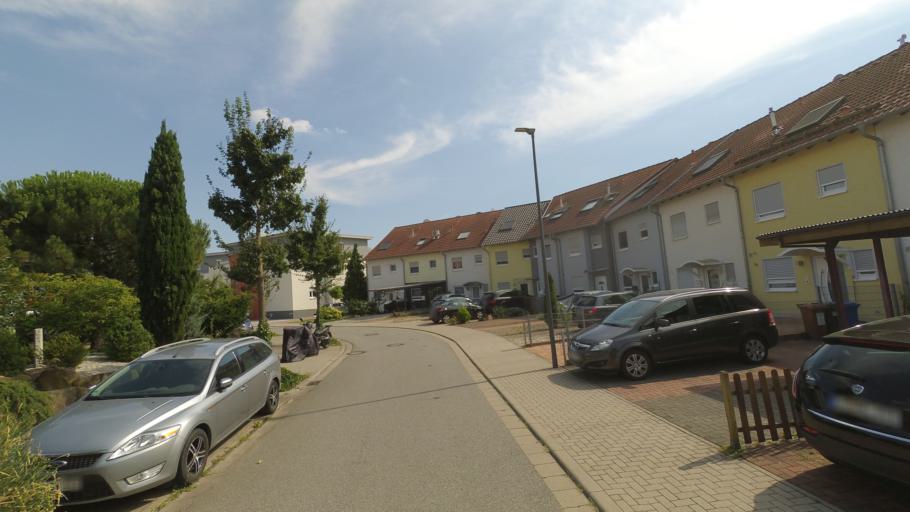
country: DE
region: Rheinland-Pfalz
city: Frankenthal
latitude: 49.5051
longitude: 8.3836
